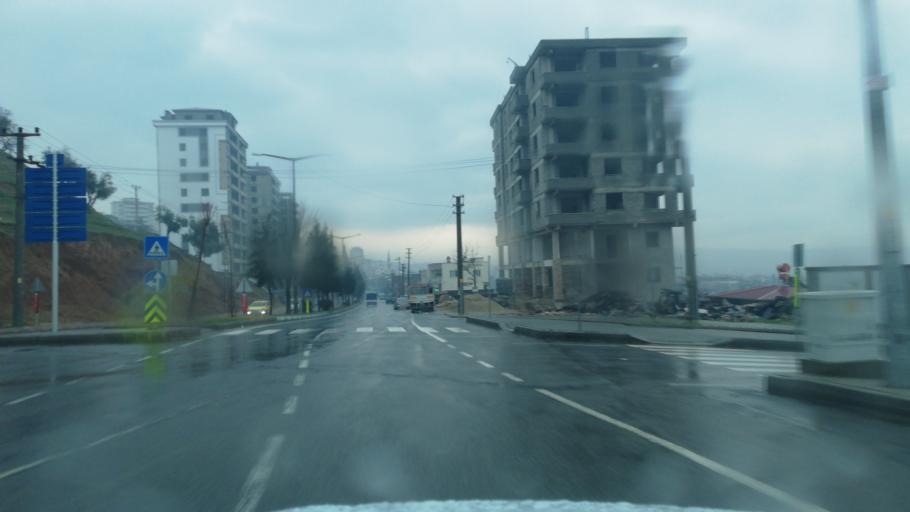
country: TR
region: Kahramanmaras
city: Kahramanmaras
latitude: 37.5818
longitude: 36.9569
